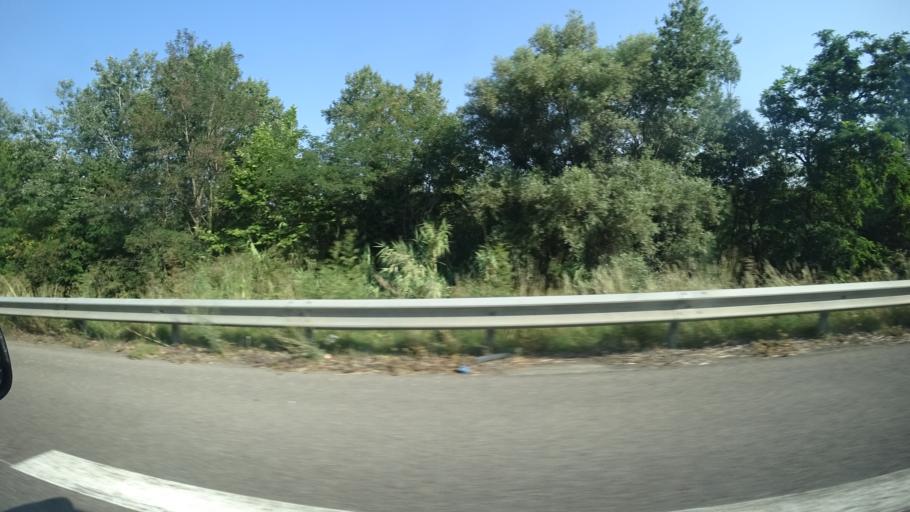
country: FR
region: Languedoc-Roussillon
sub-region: Departement des Pyrenees-Orientales
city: Le Soler
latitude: 42.6835
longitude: 2.7839
